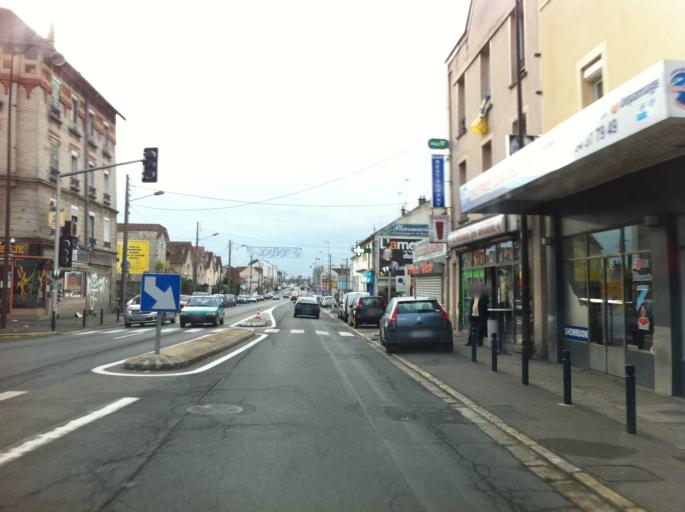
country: FR
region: Ile-de-France
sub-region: Departement de Seine-et-Marne
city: Dammarie-les-Lys
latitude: 48.5239
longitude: 2.6464
